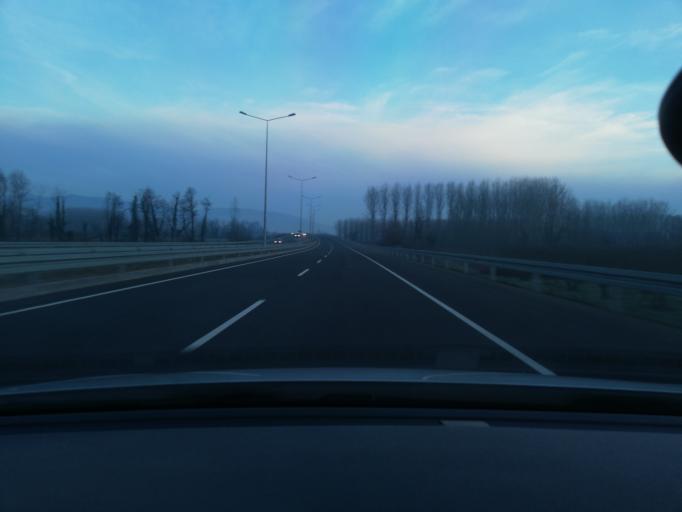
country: TR
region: Duzce
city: Duzce
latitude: 40.8127
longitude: 31.1692
